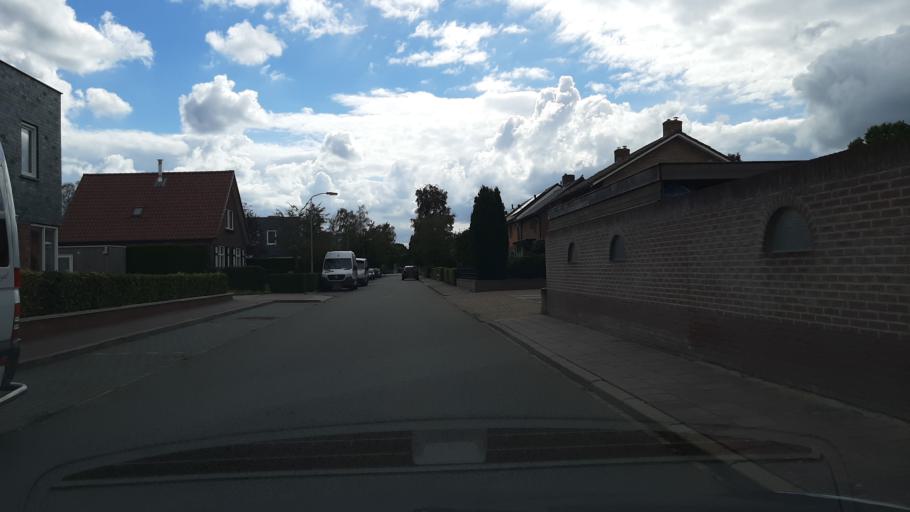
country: NL
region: Gelderland
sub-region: Gemeente Ermelo
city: Ermelo
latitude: 52.2968
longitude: 5.6277
